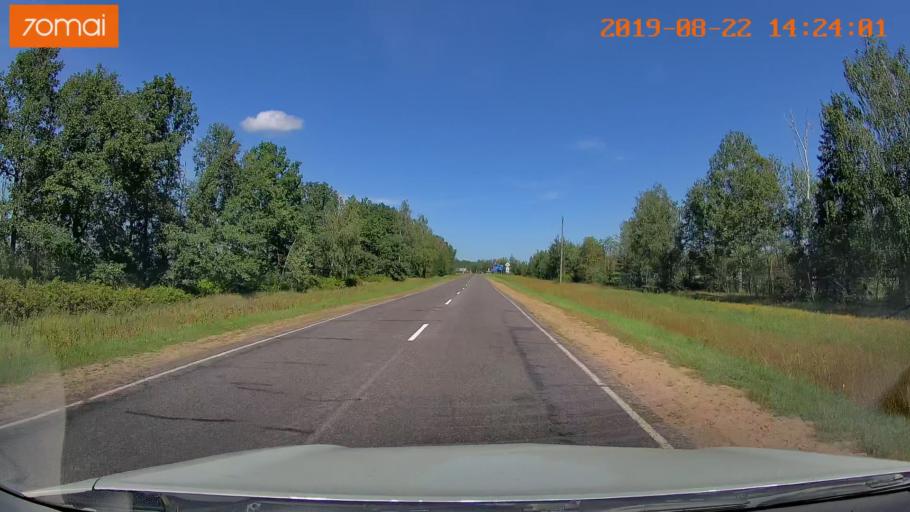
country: BY
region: Mogilev
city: Asipovichy
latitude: 53.2952
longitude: 28.5929
